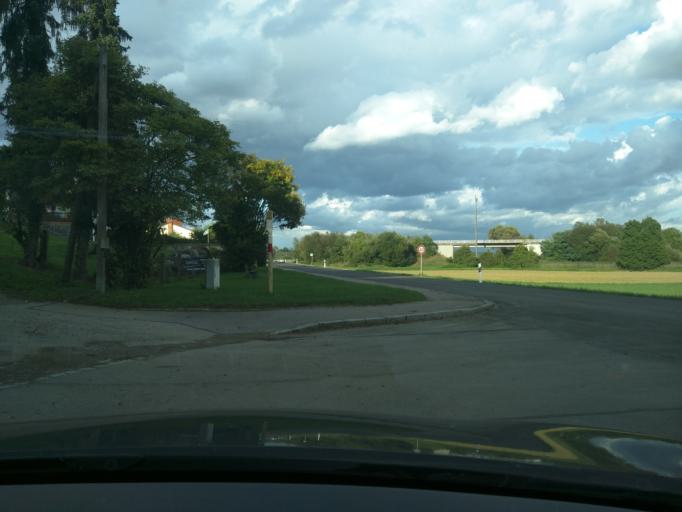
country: DE
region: Bavaria
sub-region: Upper Palatinate
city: Schwandorf in Bayern
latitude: 49.3436
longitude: 12.0928
